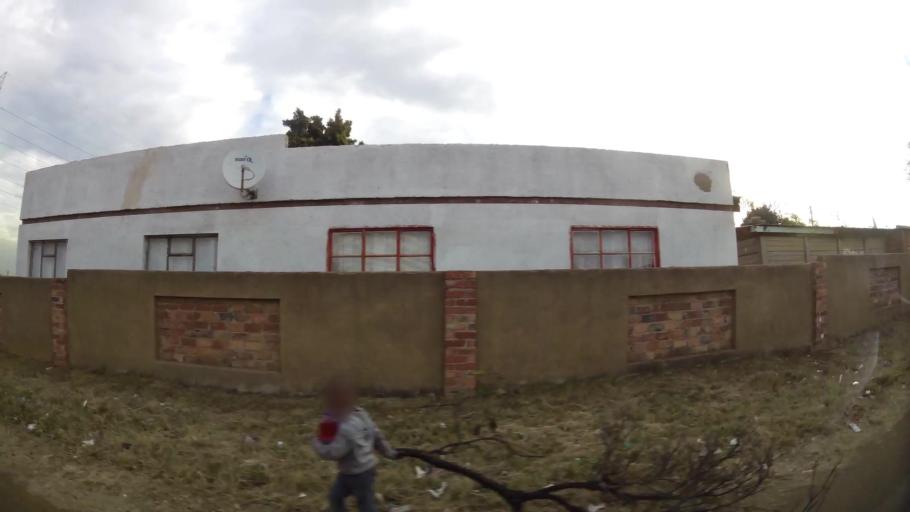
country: ZA
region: Gauteng
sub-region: City of Tshwane Metropolitan Municipality
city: Pretoria
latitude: -25.7133
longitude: 28.3253
